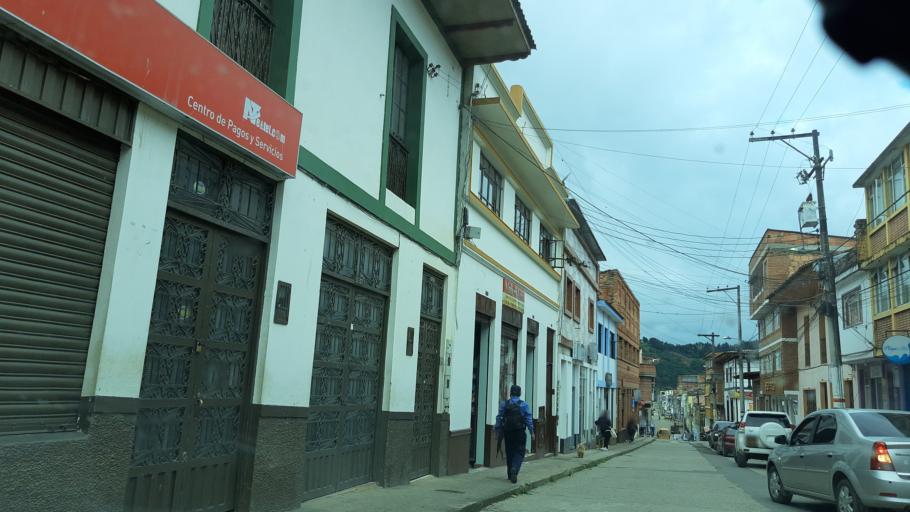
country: CO
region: Boyaca
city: Garagoa
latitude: 5.0825
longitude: -73.3632
